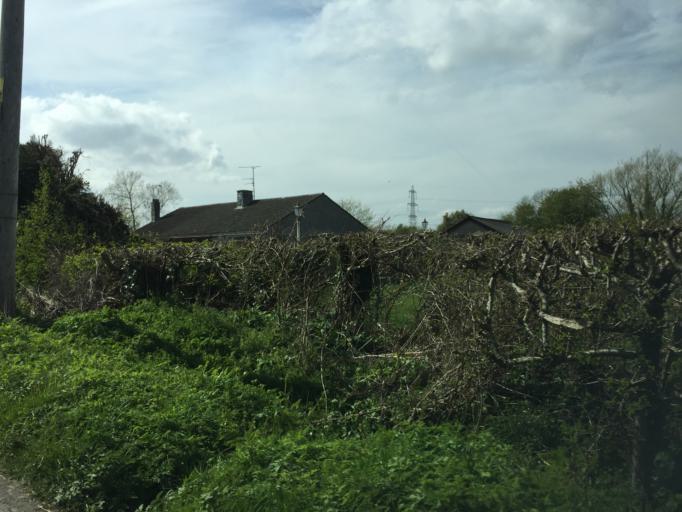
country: GB
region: England
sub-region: South Gloucestershire
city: Severn Beach
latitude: 51.5588
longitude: -2.6251
